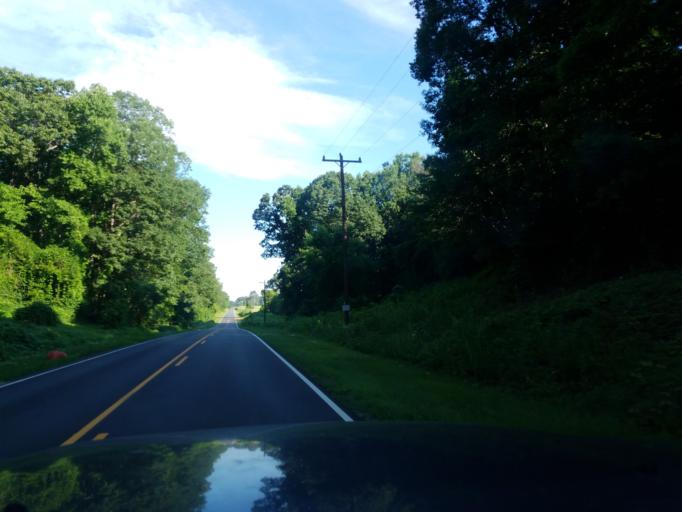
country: US
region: North Carolina
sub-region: Granville County
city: Butner
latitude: 36.1636
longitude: -78.7815
